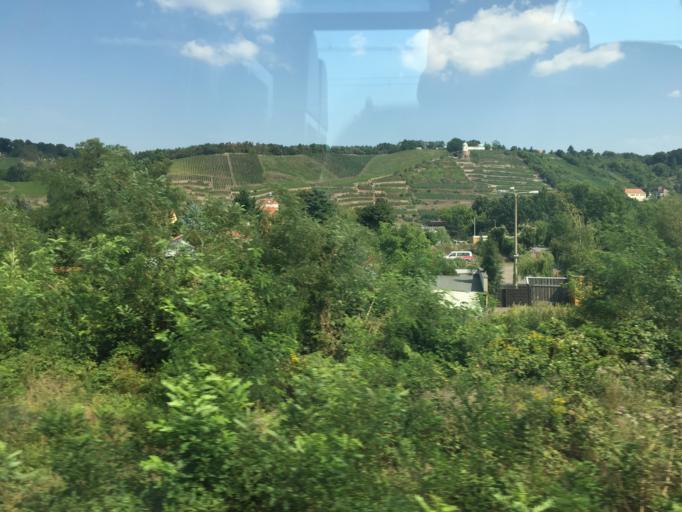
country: DE
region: Saxony
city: Coswig
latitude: 51.1115
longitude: 13.6172
